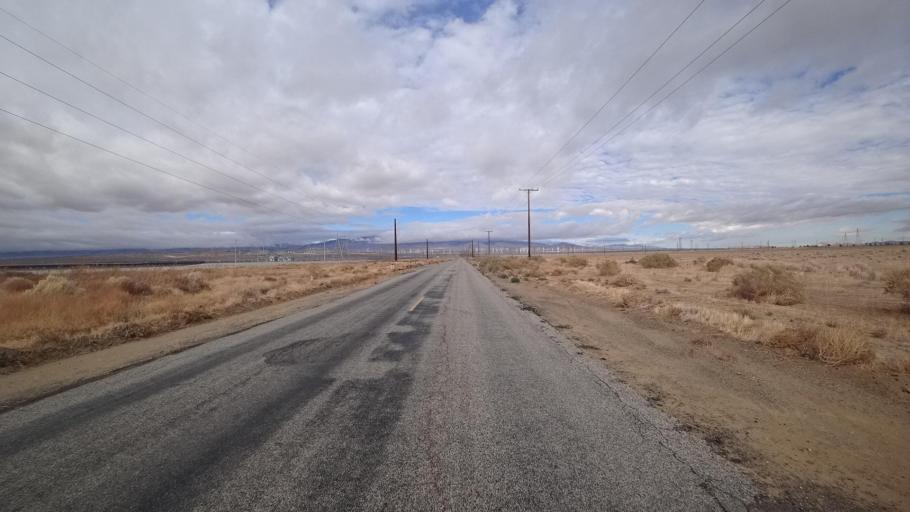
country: US
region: California
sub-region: Los Angeles County
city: Green Valley
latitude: 34.8209
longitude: -118.4317
